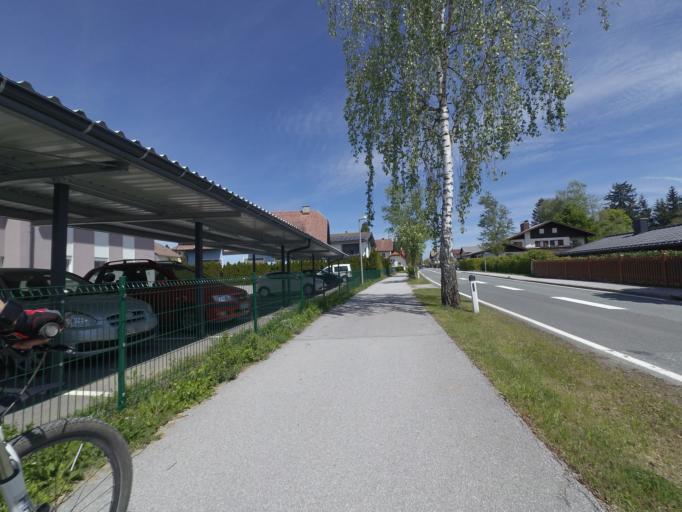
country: AT
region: Salzburg
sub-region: Politischer Bezirk Salzburg-Umgebung
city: Seeham
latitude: 47.9654
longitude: 13.0757
